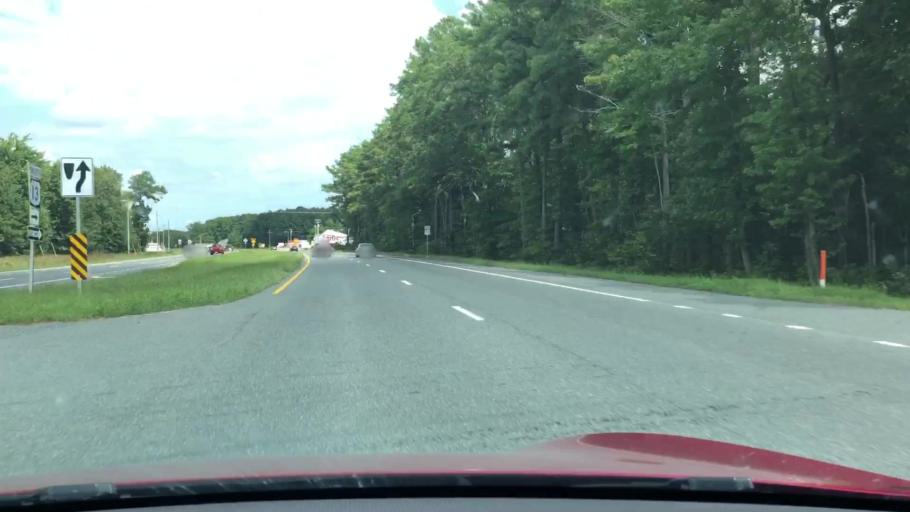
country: US
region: Virginia
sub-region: Accomack County
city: Accomac
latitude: 37.7043
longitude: -75.7019
